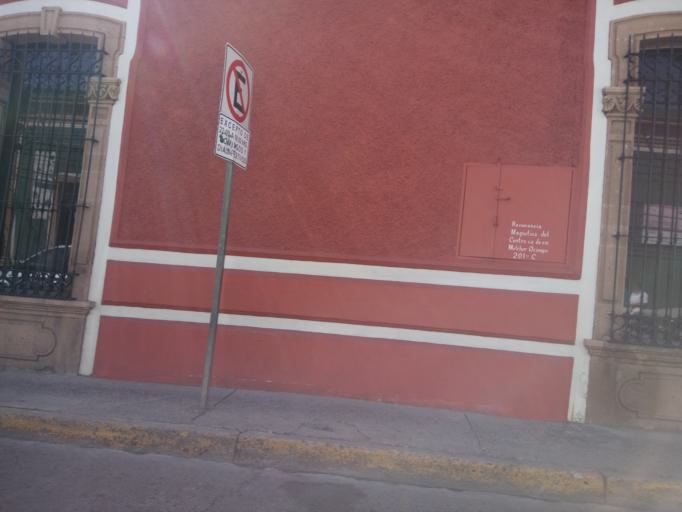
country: MX
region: Guanajuato
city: Leon
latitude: 21.1249
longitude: -101.6806
